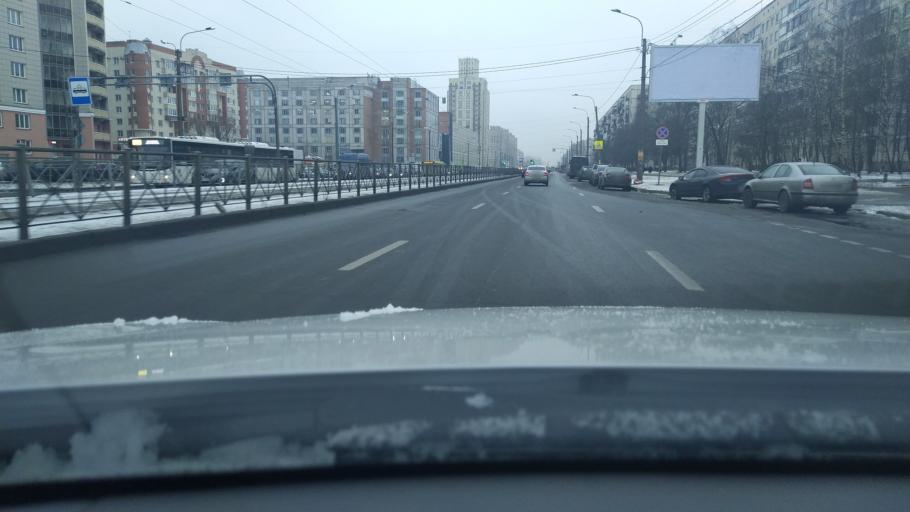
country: RU
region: St.-Petersburg
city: Grazhdanka
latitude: 60.0335
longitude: 30.4304
